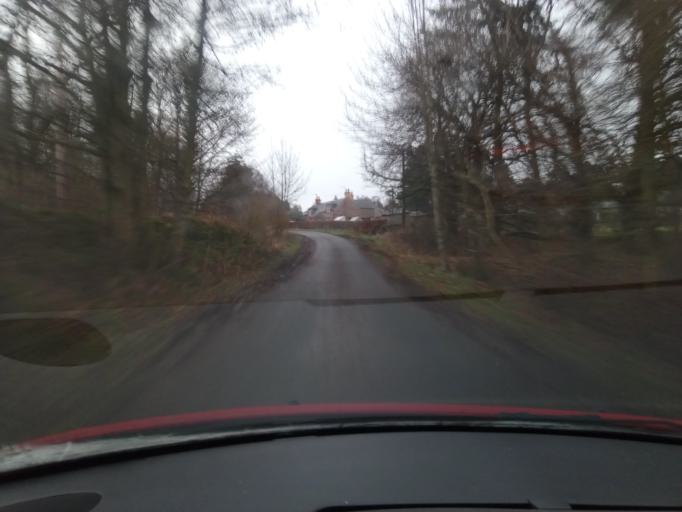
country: GB
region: Scotland
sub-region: The Scottish Borders
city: Kelso
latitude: 55.5510
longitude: -2.4319
